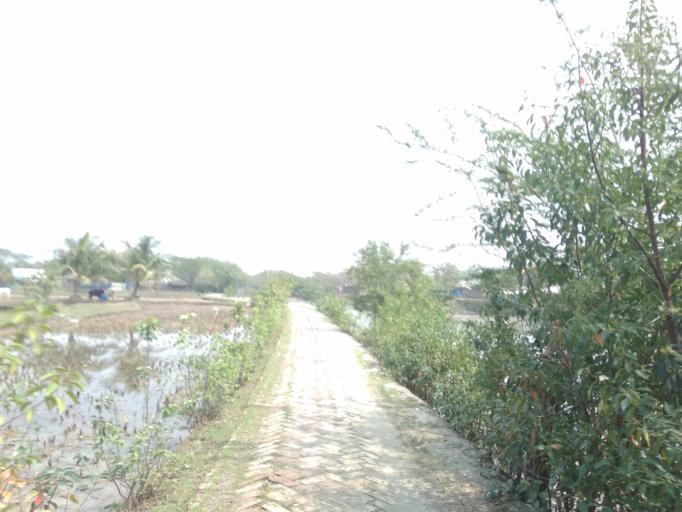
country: IN
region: West Bengal
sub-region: North 24 Parganas
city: Taki
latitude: 22.2572
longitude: 89.2573
